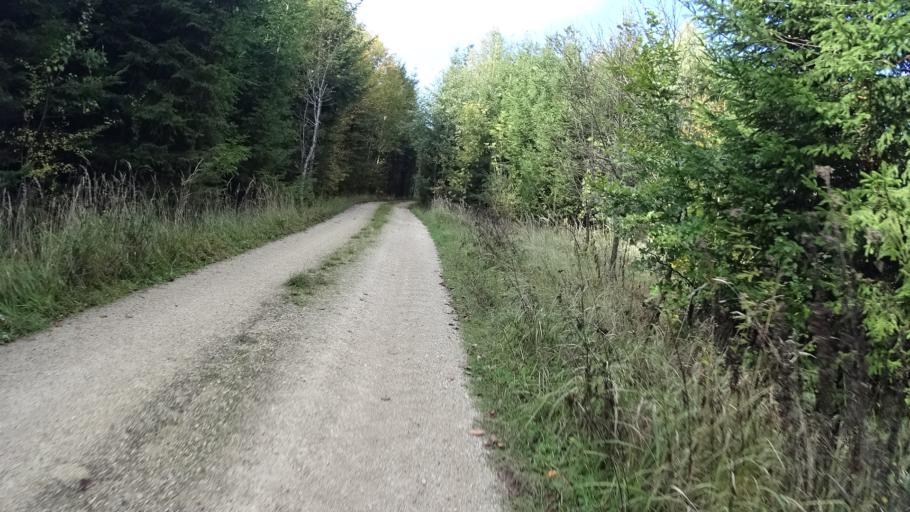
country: DE
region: Bavaria
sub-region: Upper Bavaria
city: Bohmfeld
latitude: 48.8786
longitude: 11.3845
